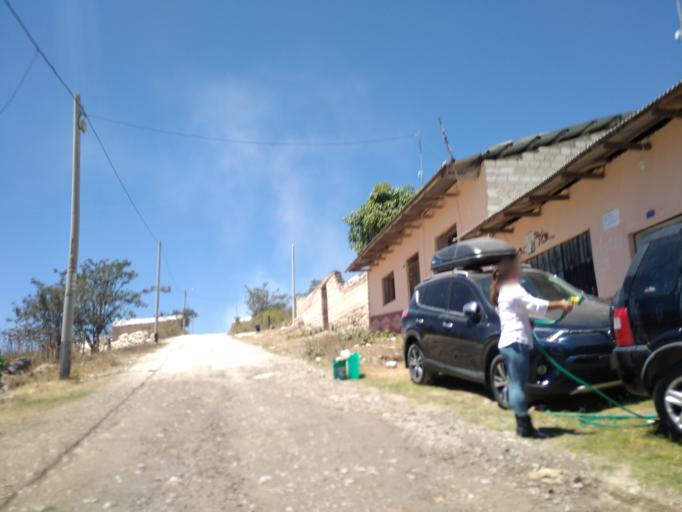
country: PE
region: Amazonas
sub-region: Provincia de Luya
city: Tingo
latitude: -6.3747
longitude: -77.9109
